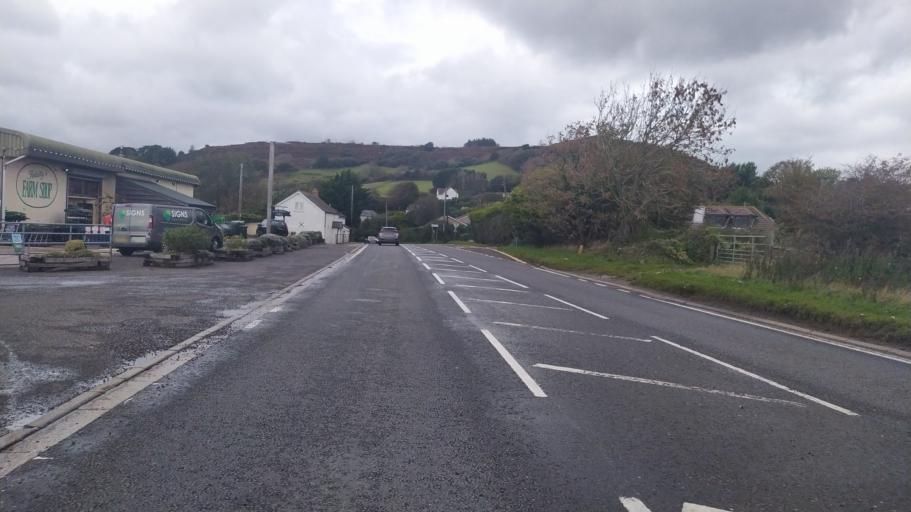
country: GB
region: England
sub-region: Dorset
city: Bridport
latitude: 50.7400
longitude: -2.8381
